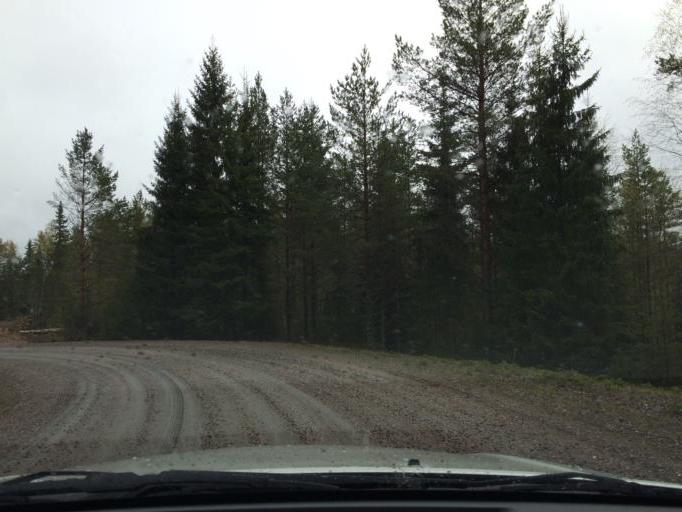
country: SE
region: OErebro
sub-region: Hallefors Kommun
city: Haellefors
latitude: 60.0151
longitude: 14.5884
